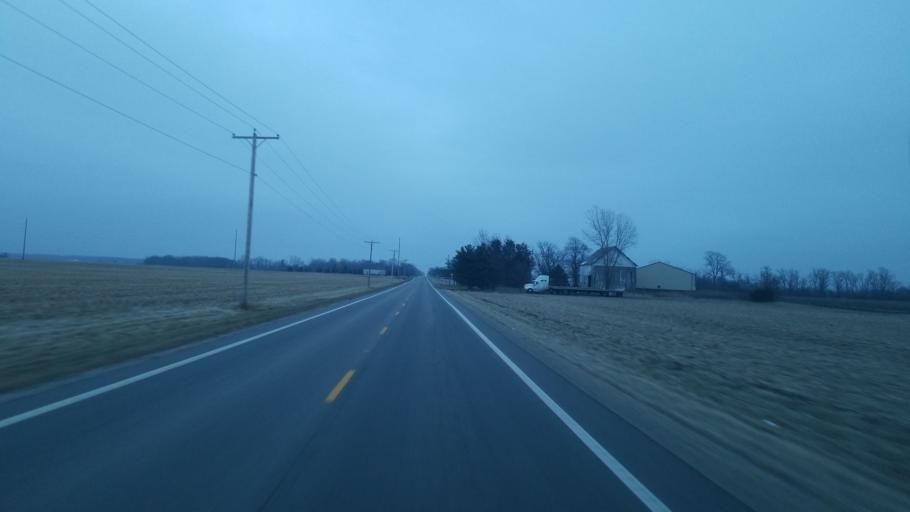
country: US
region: Ohio
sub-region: Mercer County
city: Rockford
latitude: 40.6550
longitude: -84.6378
